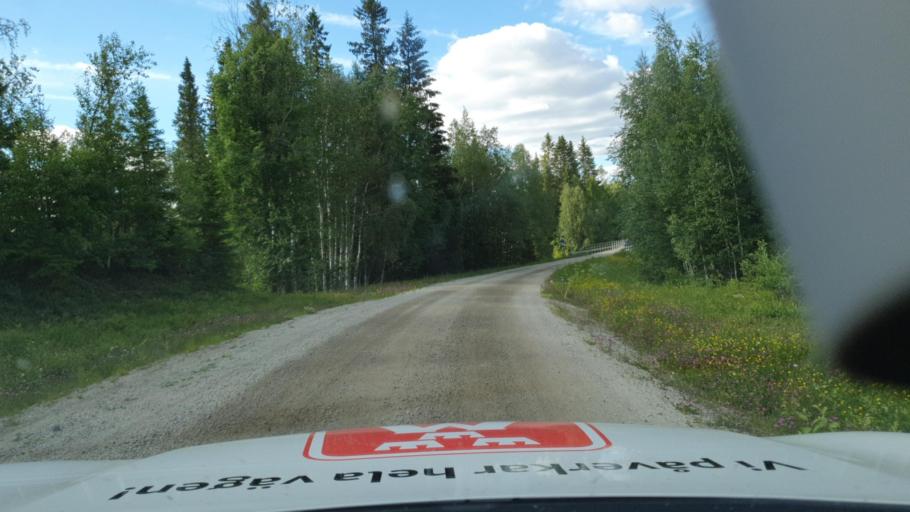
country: SE
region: Vaesterbotten
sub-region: Lycksele Kommun
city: Lycksele
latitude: 64.4728
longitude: 18.2847
